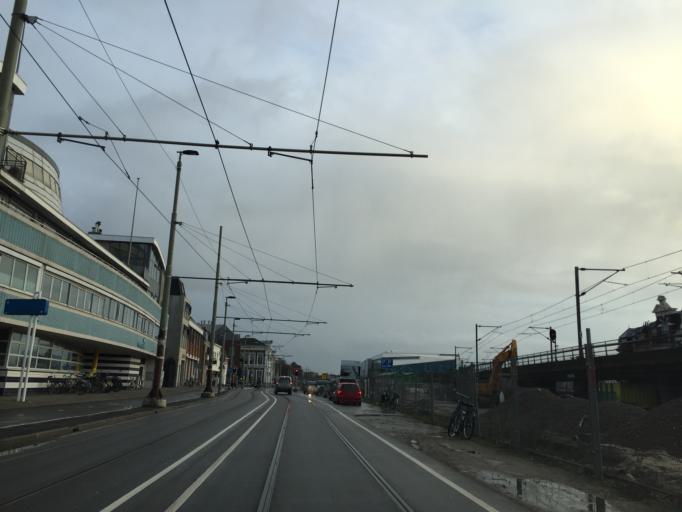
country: NL
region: South Holland
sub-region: Gemeente Delft
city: Delft
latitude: 52.0106
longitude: 4.3547
